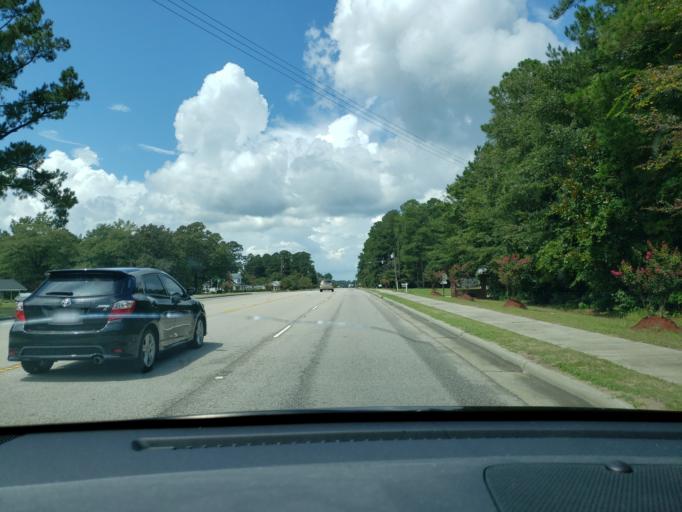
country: US
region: North Carolina
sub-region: Bladen County
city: Elizabethtown
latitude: 34.6505
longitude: -78.7130
